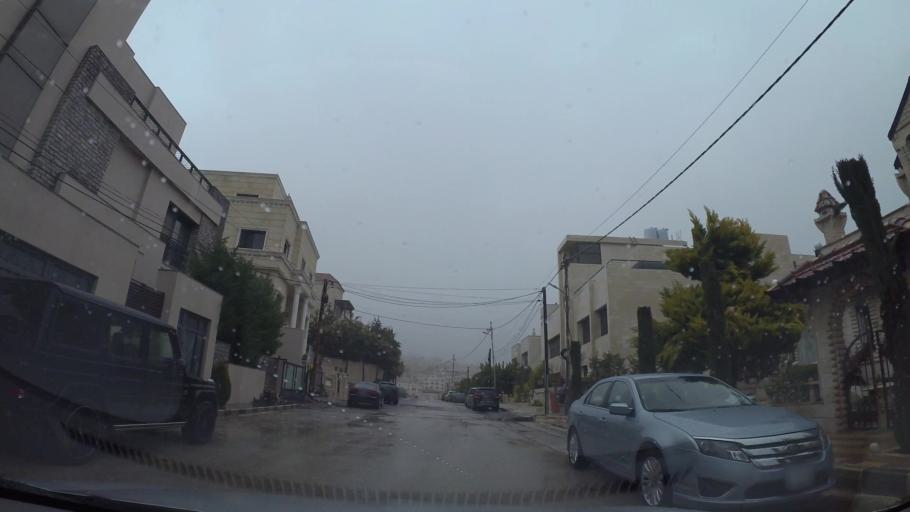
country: JO
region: Amman
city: Al Jubayhah
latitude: 32.0085
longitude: 35.8311
